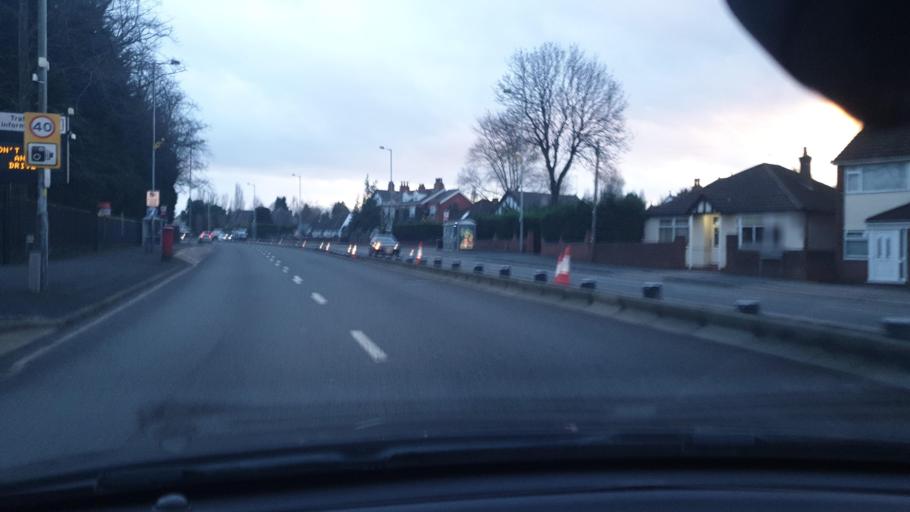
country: GB
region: England
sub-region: Wolverhampton
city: Wolverhampton
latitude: 52.6103
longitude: -2.1309
